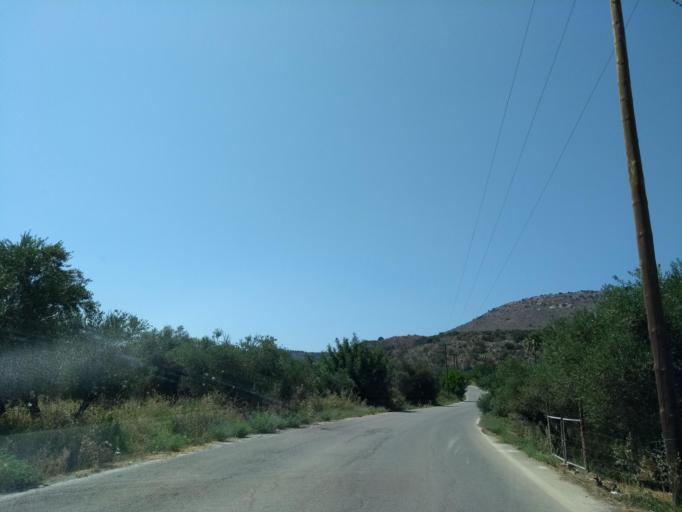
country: GR
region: Crete
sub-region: Nomos Chanias
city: Georgioupolis
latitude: 35.3765
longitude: 24.2463
